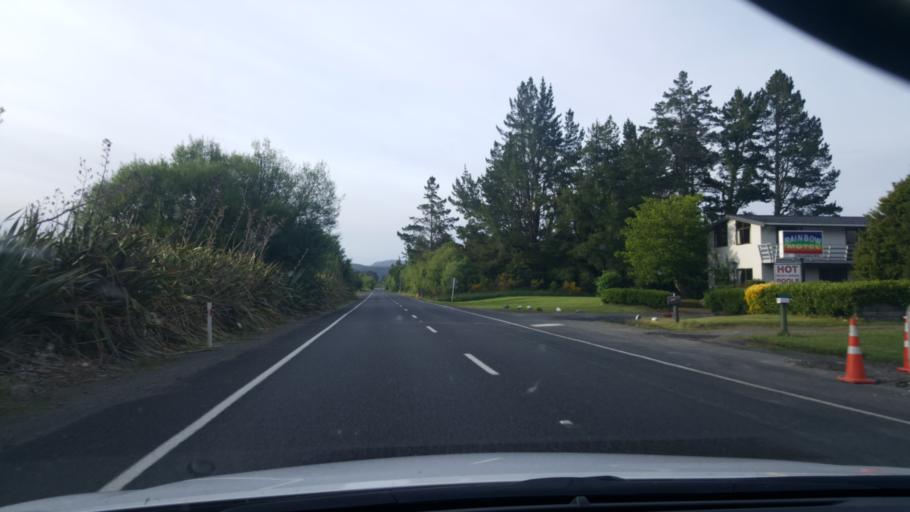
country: NZ
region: Waikato
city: Turangi
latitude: -38.9710
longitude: 175.7699
